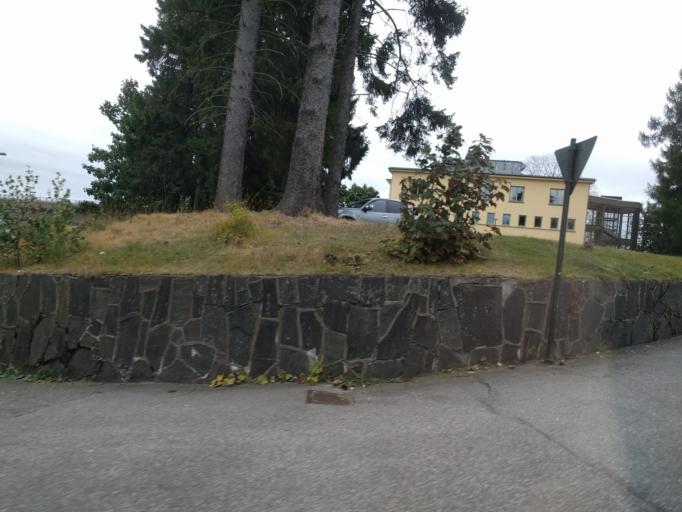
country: NO
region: Vest-Agder
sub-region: Kristiansand
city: Kristiansand
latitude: 58.1451
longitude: 7.9807
